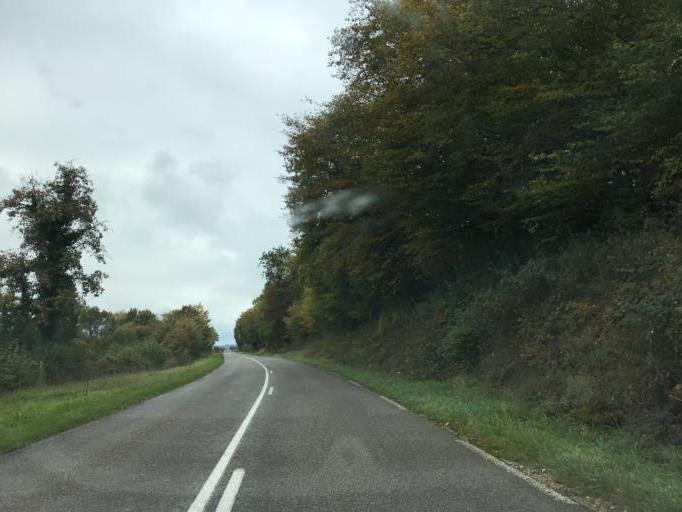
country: FR
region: Franche-Comte
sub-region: Departement du Jura
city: Arinthod
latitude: 46.4603
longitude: 5.5564
